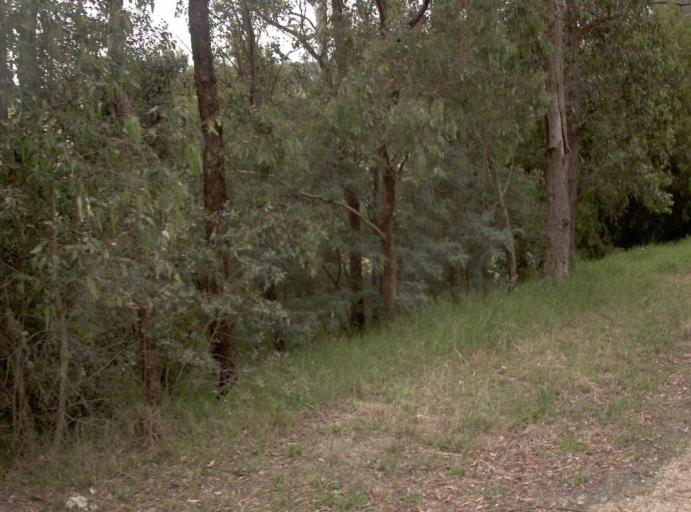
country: AU
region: Victoria
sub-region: East Gippsland
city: Bairnsdale
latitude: -37.7779
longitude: 147.5979
